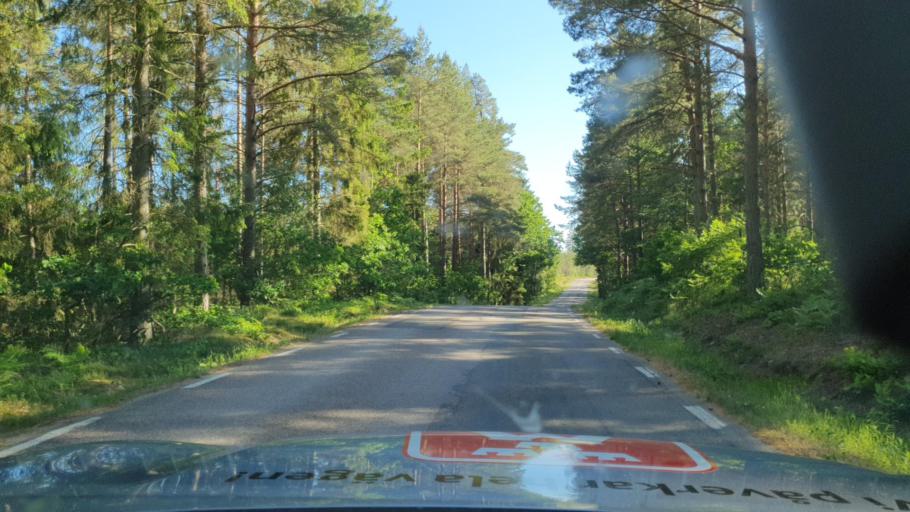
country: SE
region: Kalmar
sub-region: Torsas Kommun
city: Torsas
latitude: 56.4922
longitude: 16.1019
